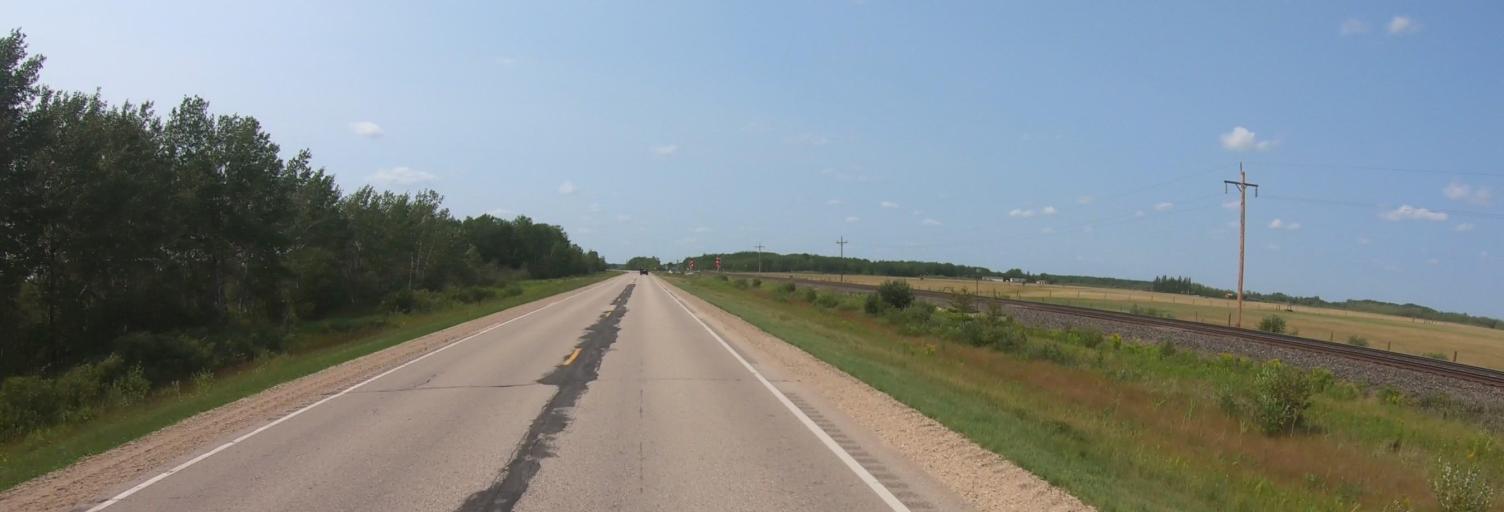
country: US
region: Minnesota
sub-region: Lake of the Woods County
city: Baudette
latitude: 48.7362
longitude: -94.8200
